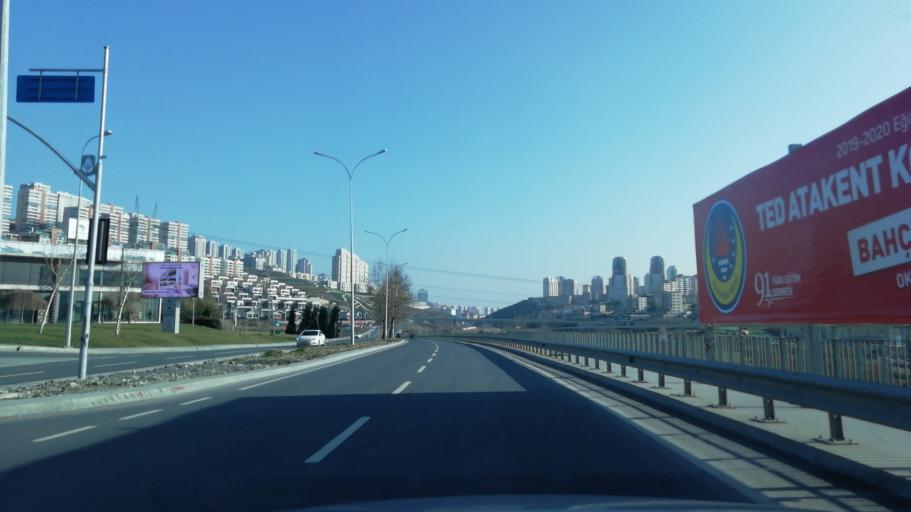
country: TR
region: Istanbul
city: Esenyurt
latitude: 41.0856
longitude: 28.6781
